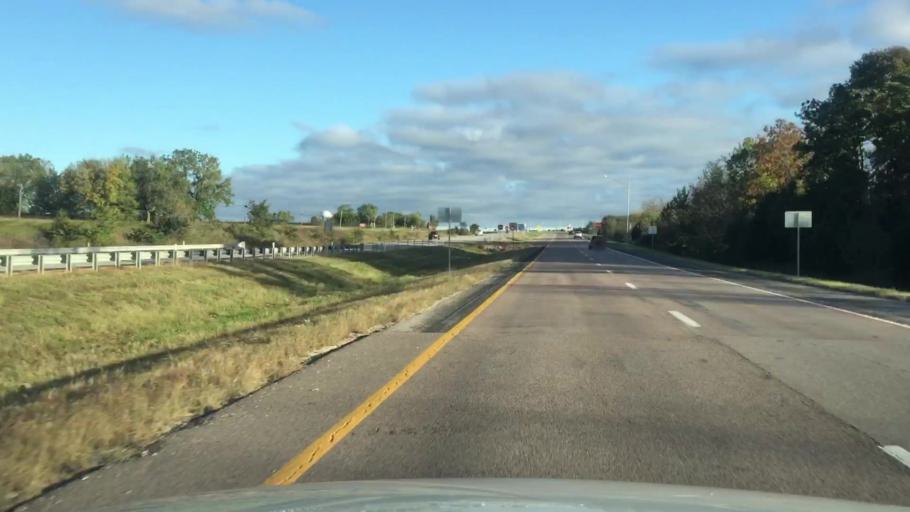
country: US
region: Missouri
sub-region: Boone County
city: Ashland
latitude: 38.8543
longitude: -92.2491
